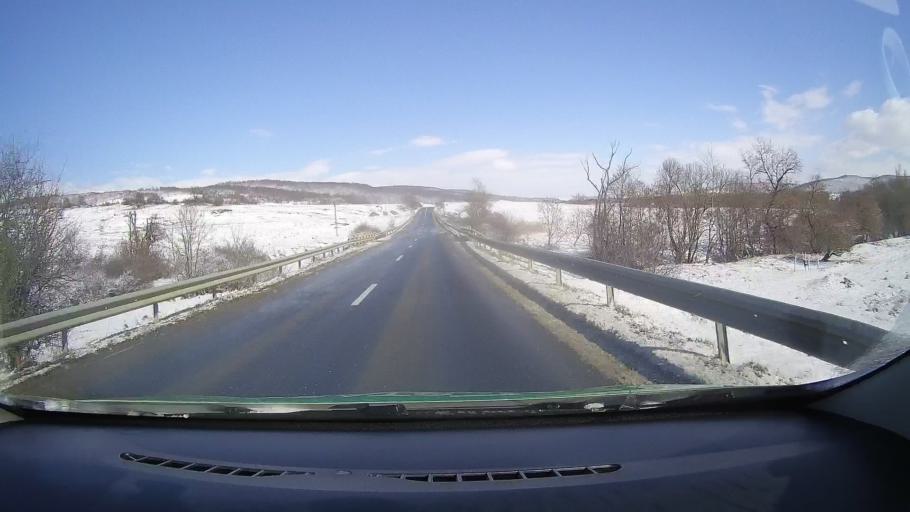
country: RO
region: Sibiu
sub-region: Comuna Rosia
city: Rosia
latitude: 45.8207
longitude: 24.3808
